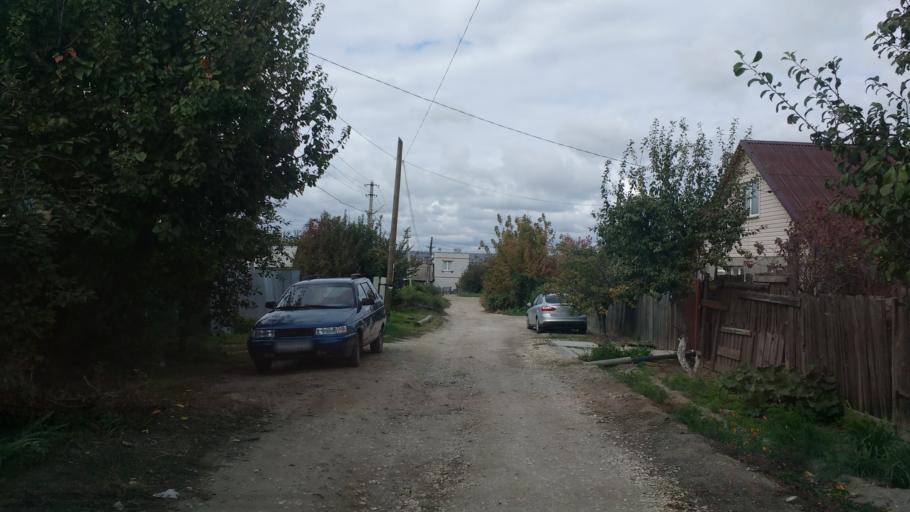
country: RU
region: Volgograd
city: Vodstroy
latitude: 48.7806
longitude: 44.5395
